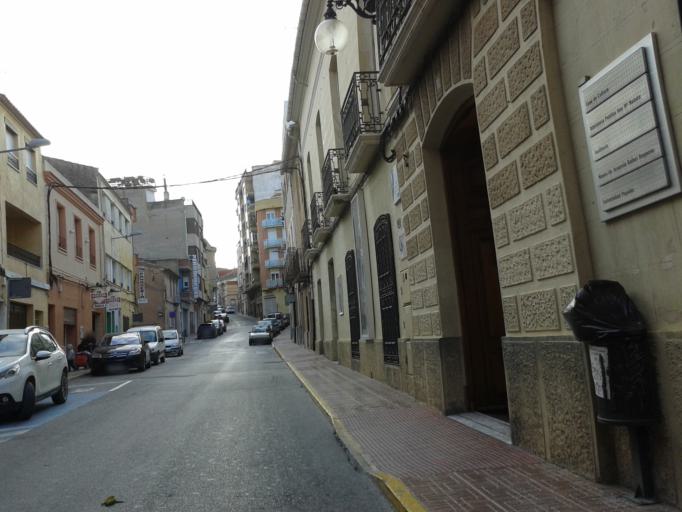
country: ES
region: Castille-La Mancha
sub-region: Provincia de Albacete
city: Caudete
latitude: 38.7067
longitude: -0.9886
